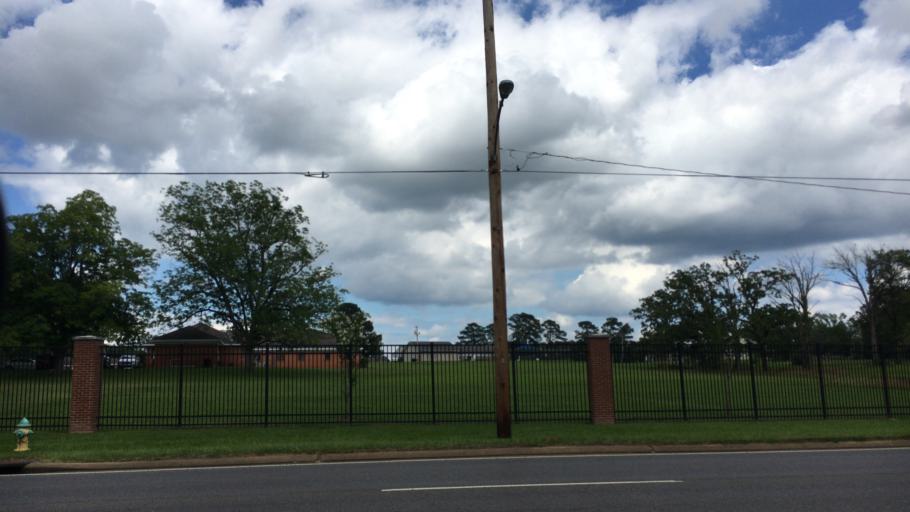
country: US
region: Louisiana
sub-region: Lincoln Parish
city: Ruston
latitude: 32.5163
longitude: -92.6387
